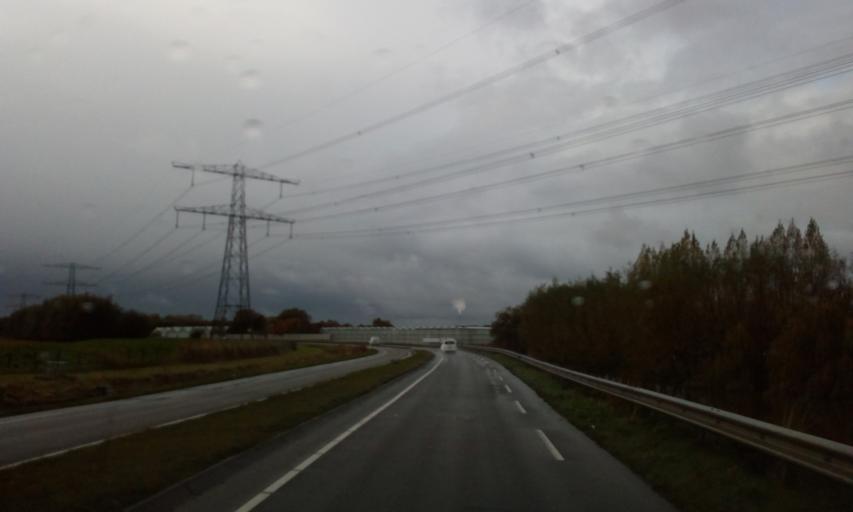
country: NL
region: South Holland
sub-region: Gemeente Westland
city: Kwintsheul
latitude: 51.9942
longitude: 4.2586
